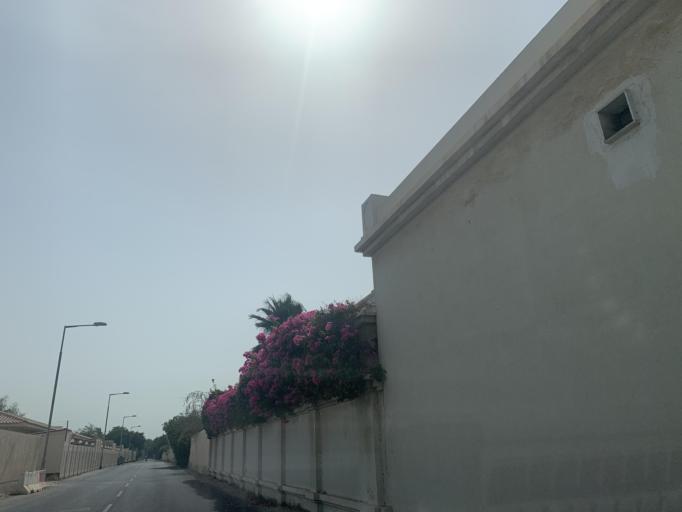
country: BH
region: Manama
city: Jidd Hafs
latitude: 26.2039
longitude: 50.4814
